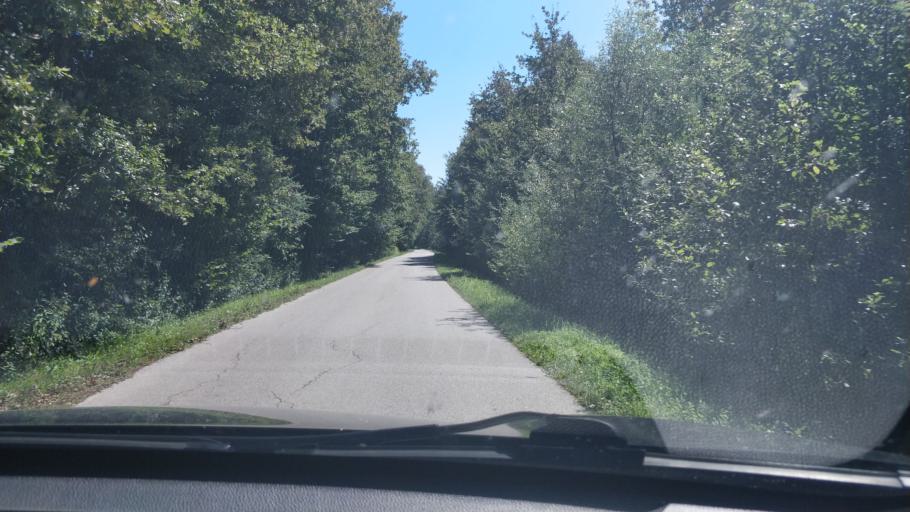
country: HR
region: Karlovacka
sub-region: Grad Karlovac
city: Karlovac
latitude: 45.4694
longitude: 15.6632
